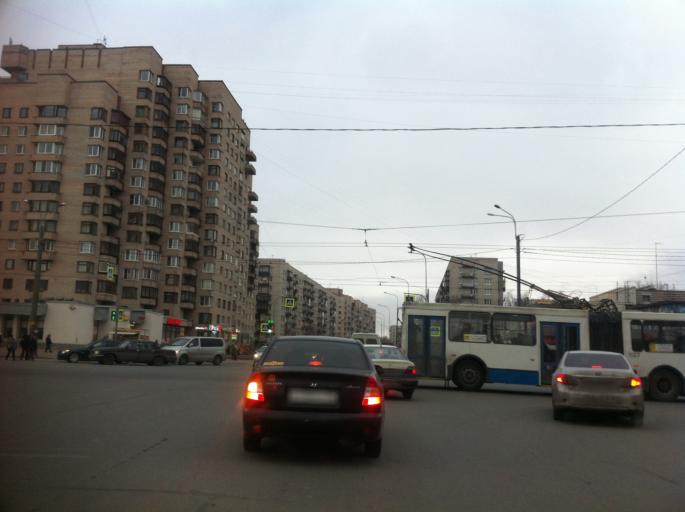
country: RU
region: St.-Petersburg
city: Dachnoye
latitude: 59.8399
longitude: 30.2387
